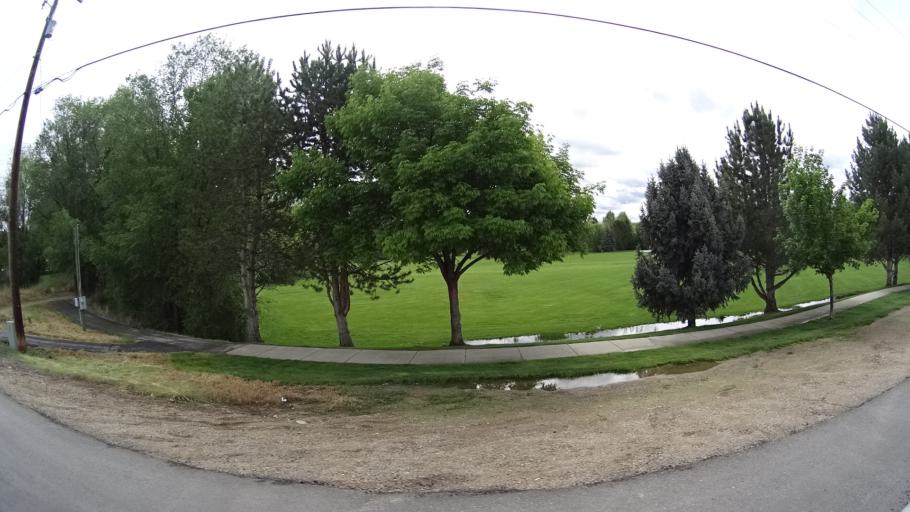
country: US
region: Idaho
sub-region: Ada County
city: Eagle
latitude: 43.7091
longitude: -116.3539
